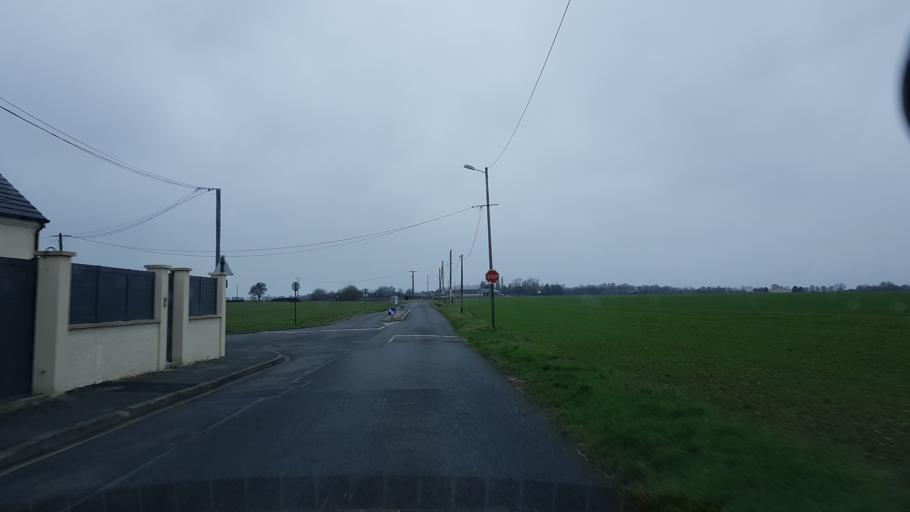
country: FR
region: Ile-de-France
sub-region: Departement de l'Essonne
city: Forges-les-Bains
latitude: 48.6497
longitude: 2.1043
